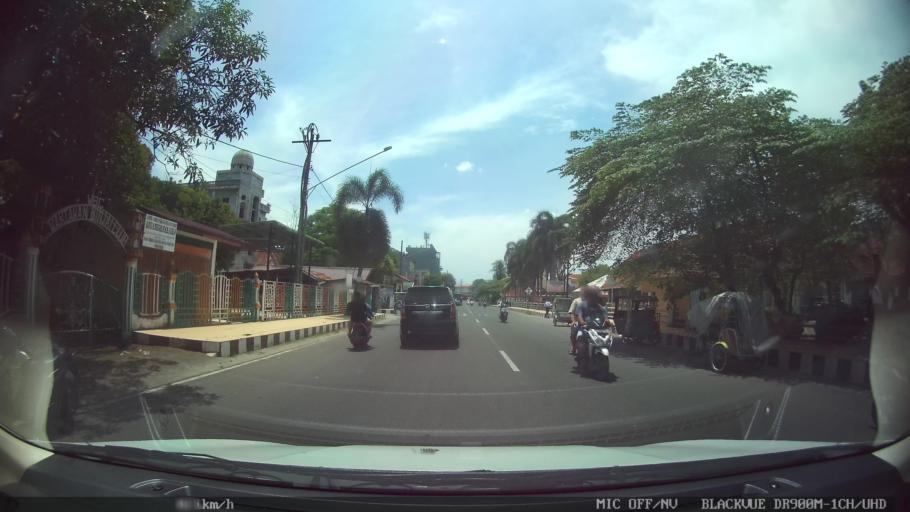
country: ID
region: North Sumatra
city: Binjai
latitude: 3.5996
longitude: 98.4883
